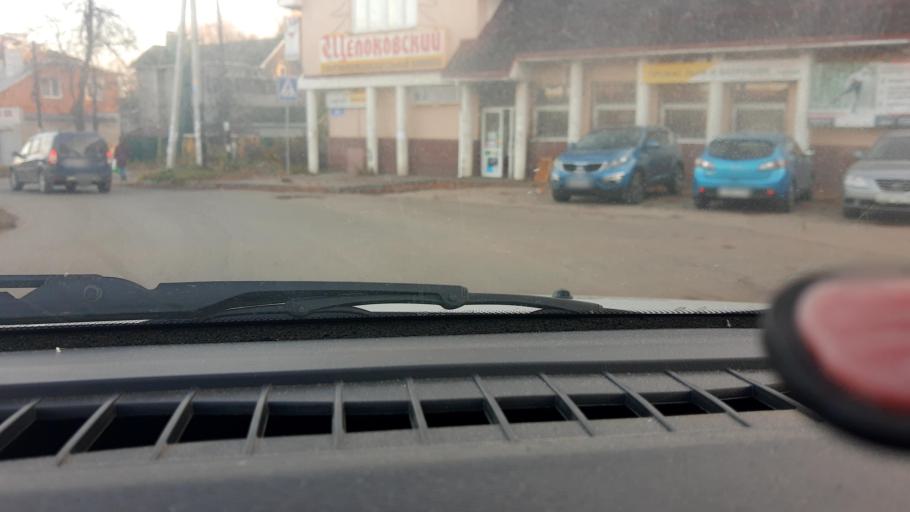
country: RU
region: Nizjnij Novgorod
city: Nizhniy Novgorod
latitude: 56.2752
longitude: 43.9978
